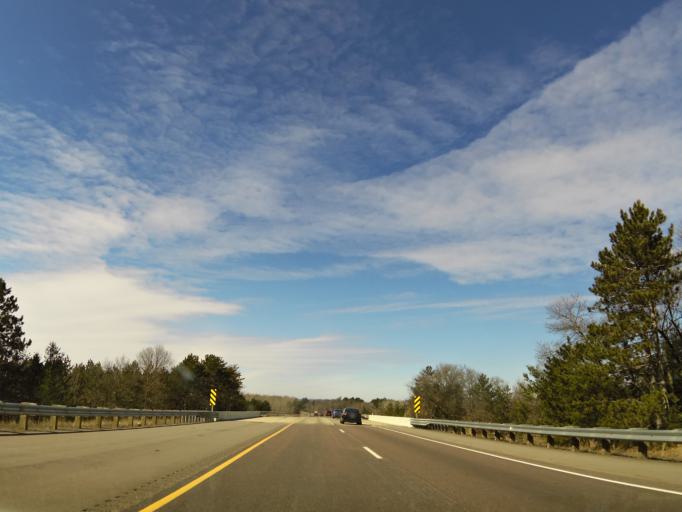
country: US
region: Wisconsin
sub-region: Jackson County
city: Black River Falls
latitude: 44.2325
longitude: -90.7108
